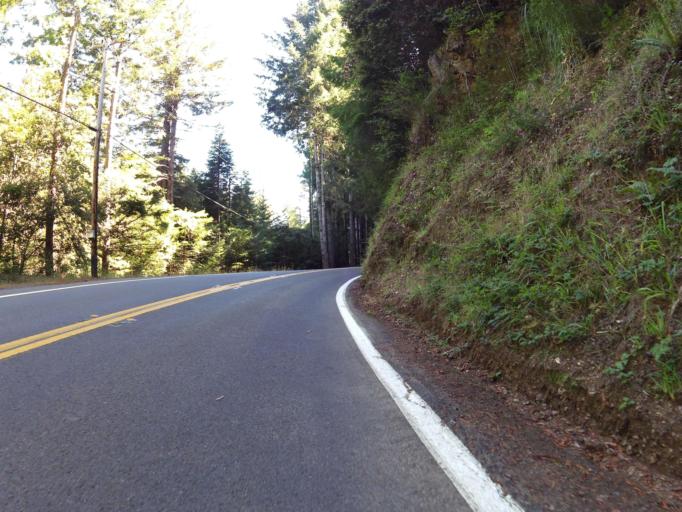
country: US
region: California
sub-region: Mendocino County
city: Fort Bragg
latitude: 39.7259
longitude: -123.8105
